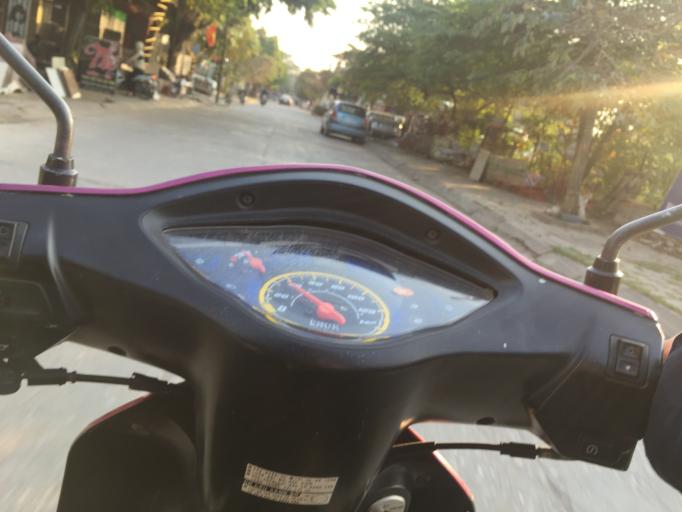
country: VN
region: Ha Noi
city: Chuc Son
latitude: 20.9175
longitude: 105.7142
